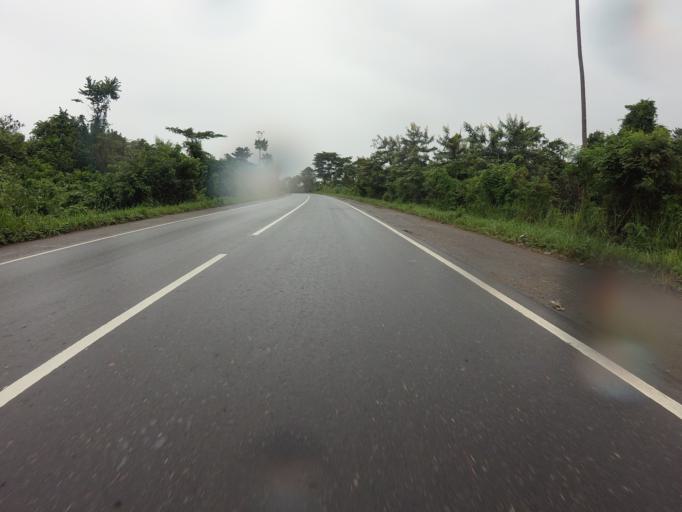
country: GH
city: Kibi
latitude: 6.1463
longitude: -0.4859
